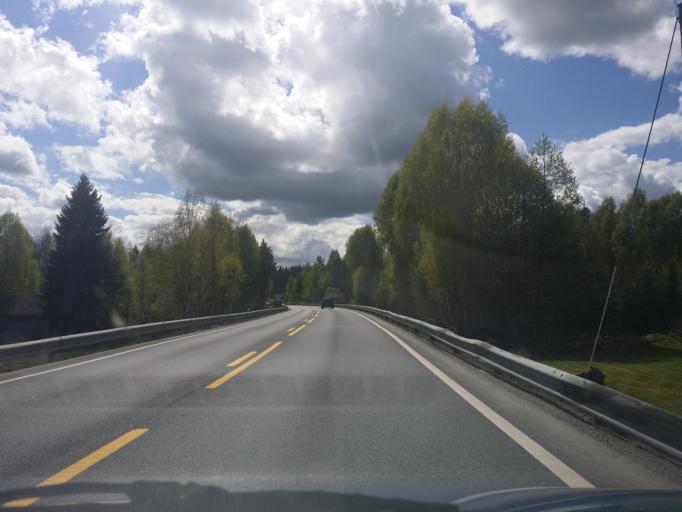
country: NO
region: Buskerud
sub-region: Modum
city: Vikersund
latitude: 59.9473
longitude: 9.9690
